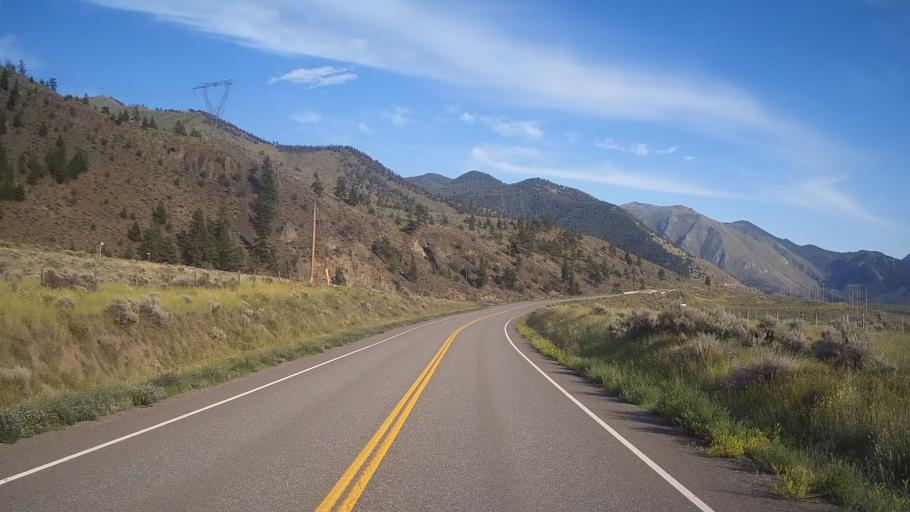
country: CA
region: British Columbia
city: Lillooet
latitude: 50.8167
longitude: -121.8535
